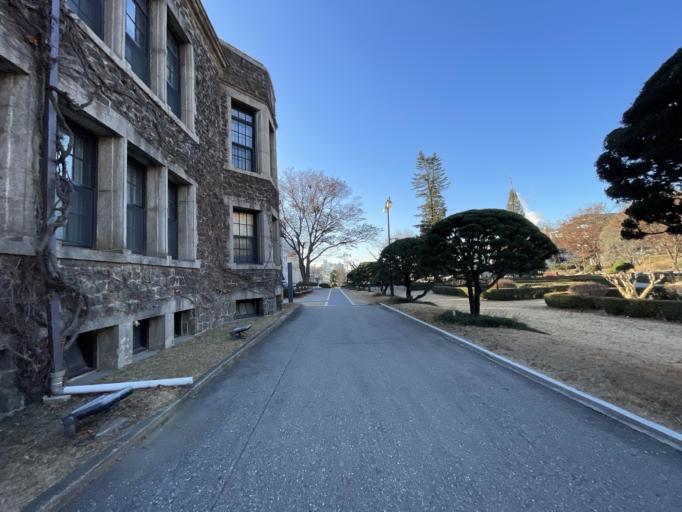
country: KR
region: Seoul
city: Seoul
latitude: 37.5659
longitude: 126.9389
